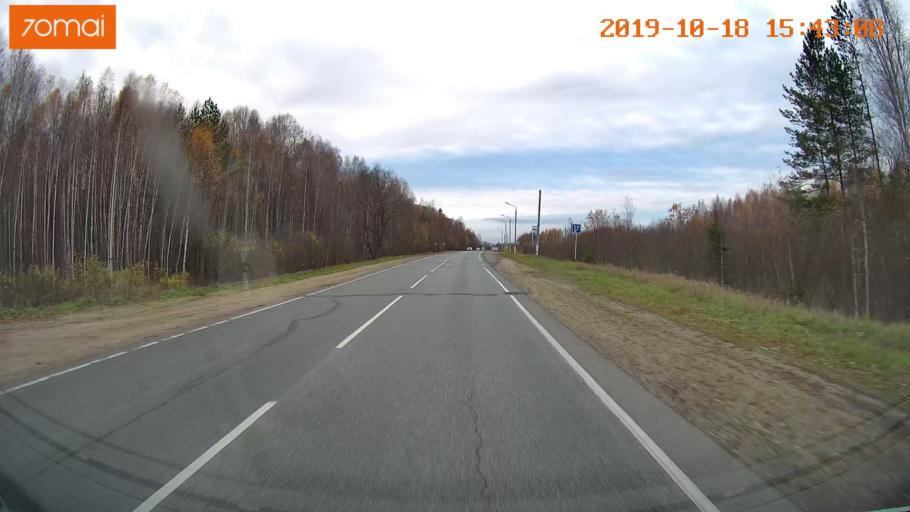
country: RU
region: Vladimir
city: Golovino
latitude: 55.9635
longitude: 40.5557
